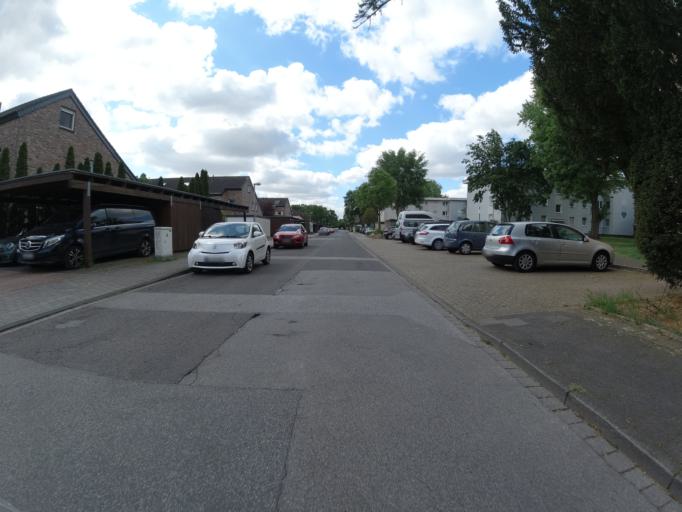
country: DE
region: North Rhine-Westphalia
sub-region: Regierungsbezirk Dusseldorf
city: Moers
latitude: 51.4008
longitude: 6.6560
